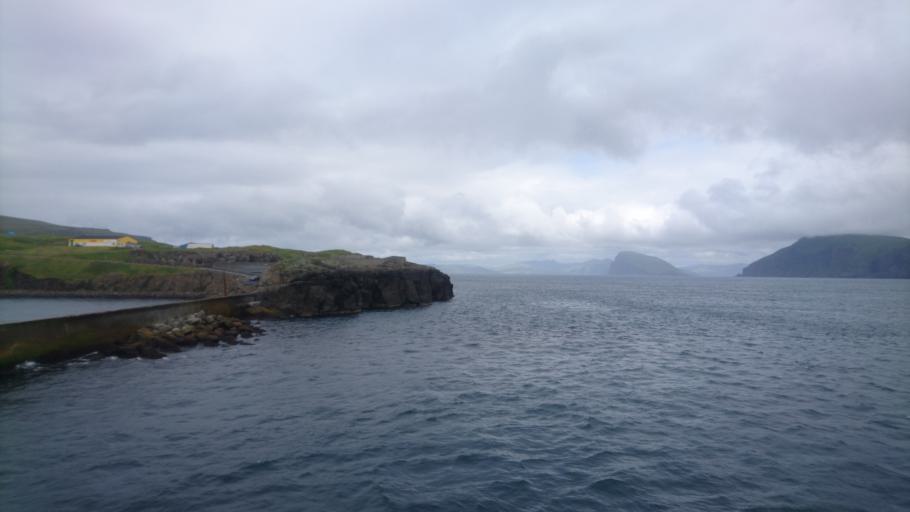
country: FO
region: Sandoy
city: Sandur
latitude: 61.9050
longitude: -6.8775
